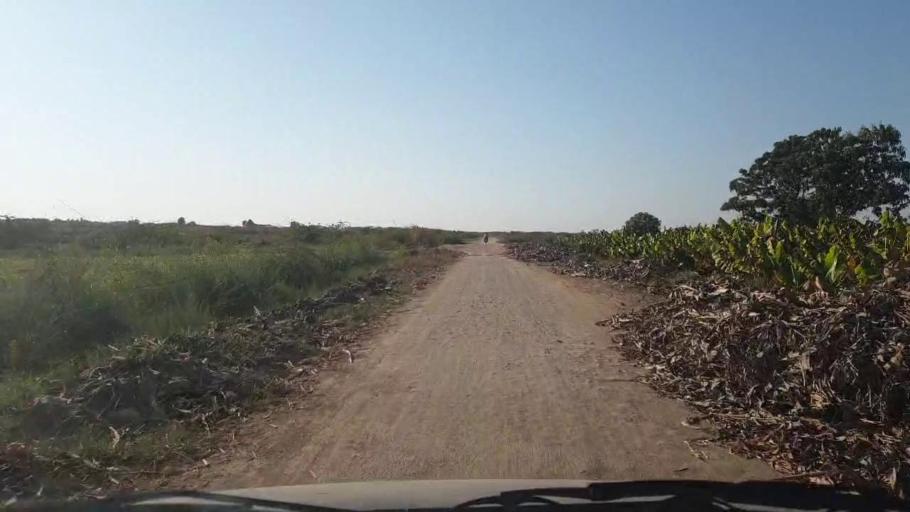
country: PK
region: Sindh
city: Samaro
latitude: 25.3594
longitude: 69.2976
